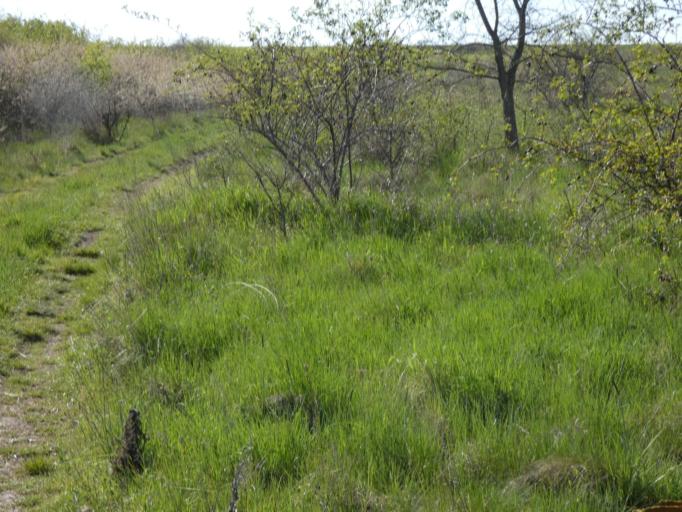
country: HU
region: Nograd
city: Bujak
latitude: 47.8894
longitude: 19.6015
